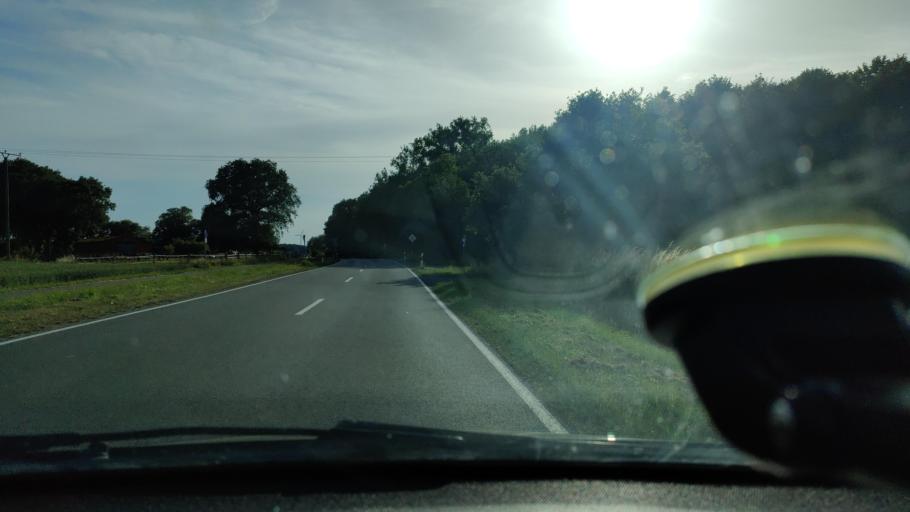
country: DE
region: North Rhine-Westphalia
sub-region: Regierungsbezirk Munster
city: Schoppingen
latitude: 52.0292
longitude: 7.2052
